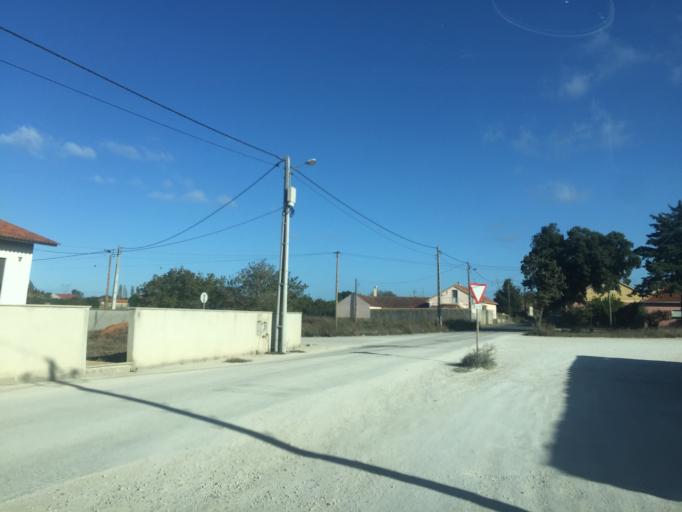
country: PT
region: Leiria
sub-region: Alcobaca
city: Benedita
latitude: 39.4351
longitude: -8.9568
